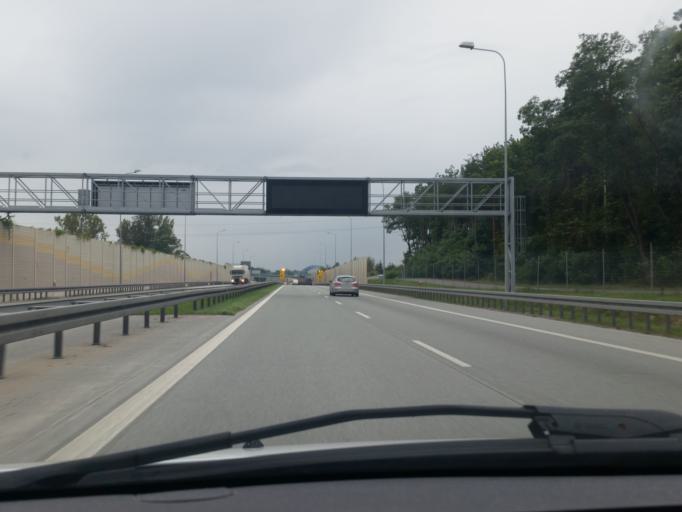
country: PL
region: Lodz Voivodeship
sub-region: Powiat skierniewicki
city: Kowiesy
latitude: 51.9238
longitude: 20.4607
